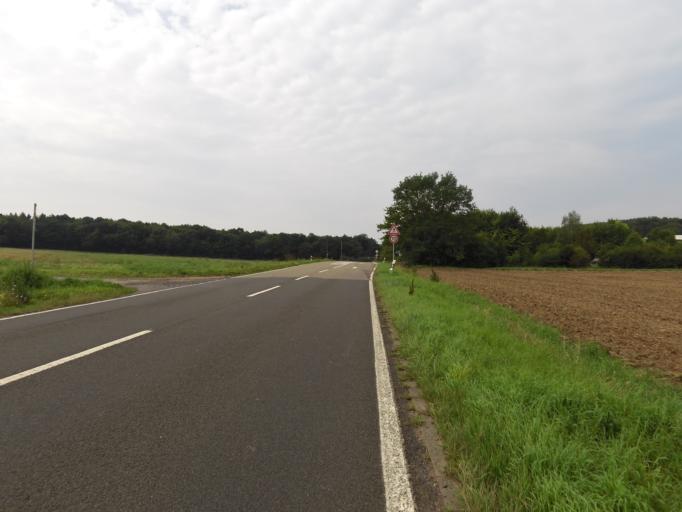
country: DE
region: Rheinland-Pfalz
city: Siefersheim
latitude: 49.7777
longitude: 7.9390
